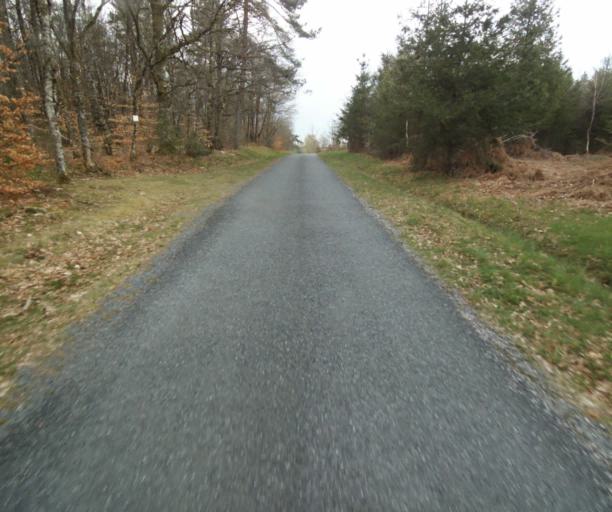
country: FR
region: Limousin
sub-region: Departement de la Correze
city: Correze
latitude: 45.2930
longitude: 1.9247
